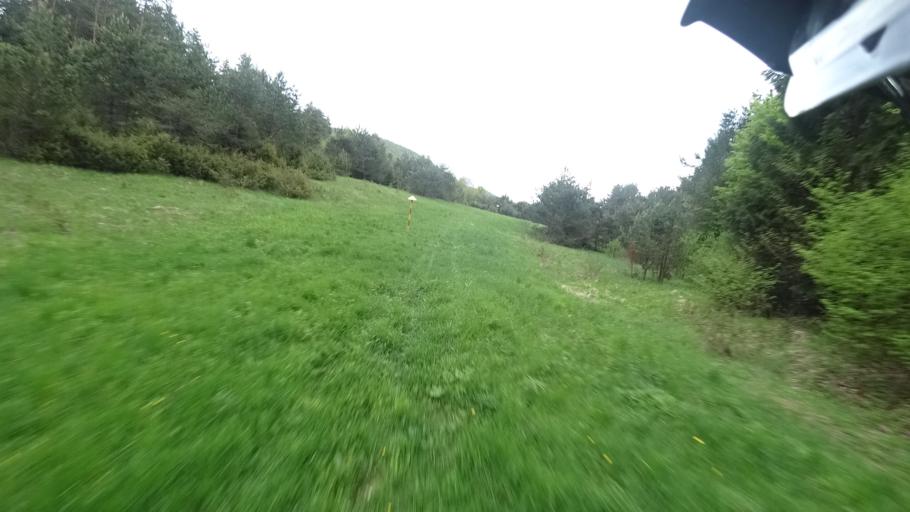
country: HR
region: Licko-Senjska
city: Jezerce
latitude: 44.8788
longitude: 15.4349
